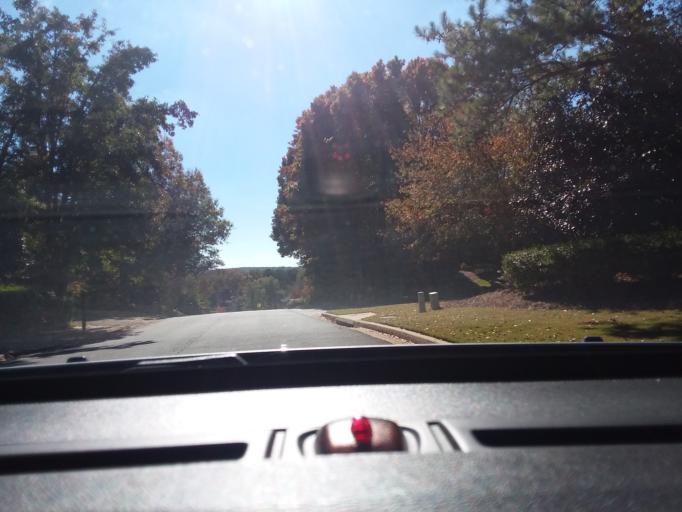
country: US
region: Georgia
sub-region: Fulton County
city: Johns Creek
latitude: 34.0283
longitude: -84.1743
